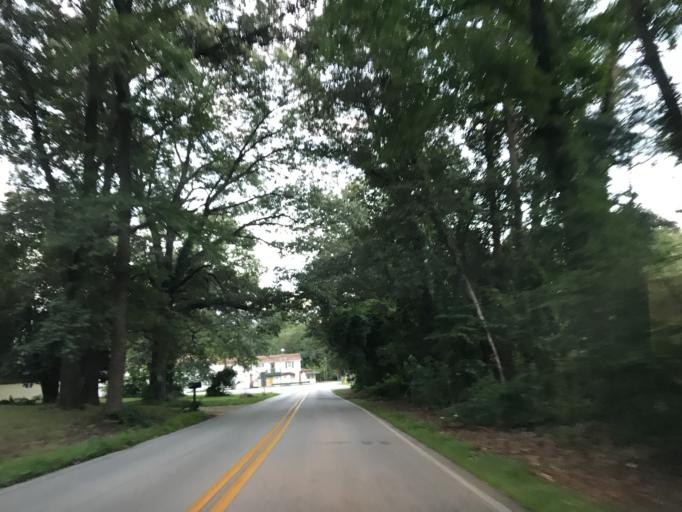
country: US
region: Maryland
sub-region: Anne Arundel County
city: Pasadena
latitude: 39.0987
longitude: -76.5701
